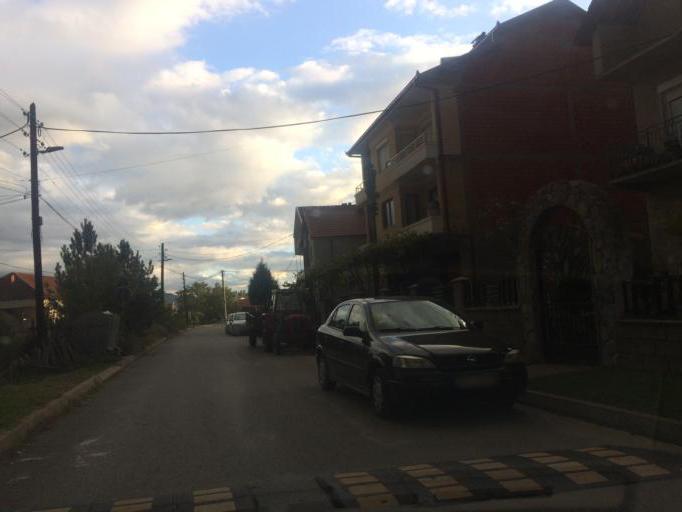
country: MK
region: Makedonska Kamenica
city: Makedonska Kamenica
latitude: 42.0256
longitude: 22.5860
